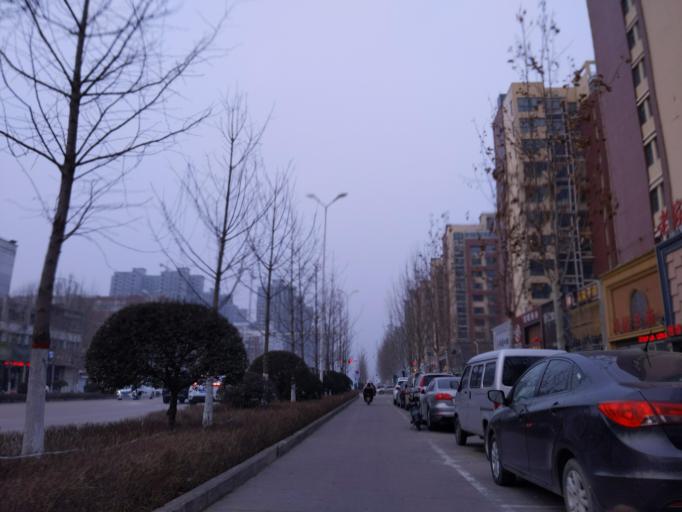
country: CN
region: Henan Sheng
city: Puyang
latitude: 35.7836
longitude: 115.0268
